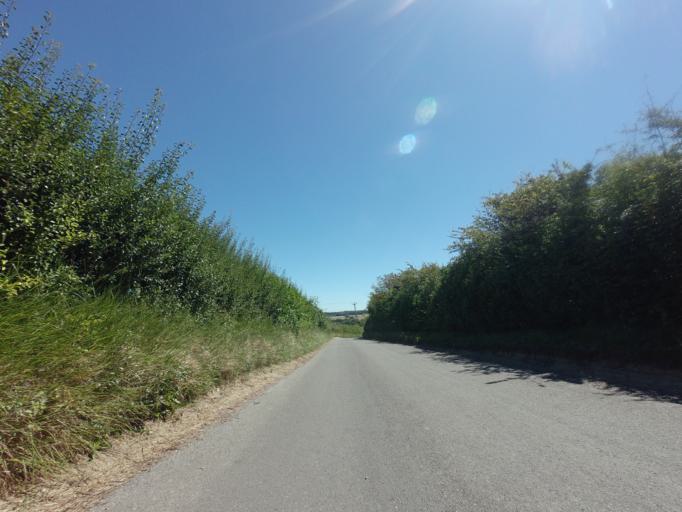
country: GB
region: England
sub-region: Kent
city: Eastry
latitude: 51.1984
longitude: 1.3347
